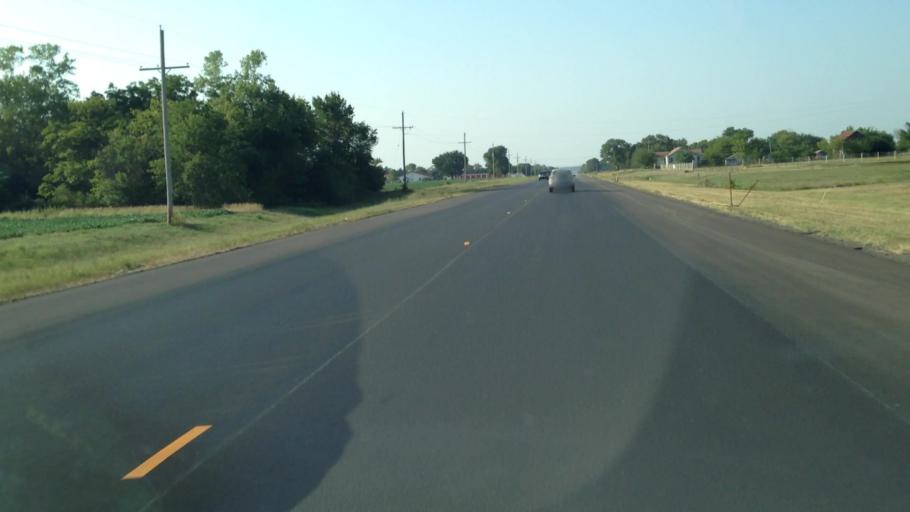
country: US
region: Kansas
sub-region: Franklin County
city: Ottawa
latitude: 38.5381
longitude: -95.2677
